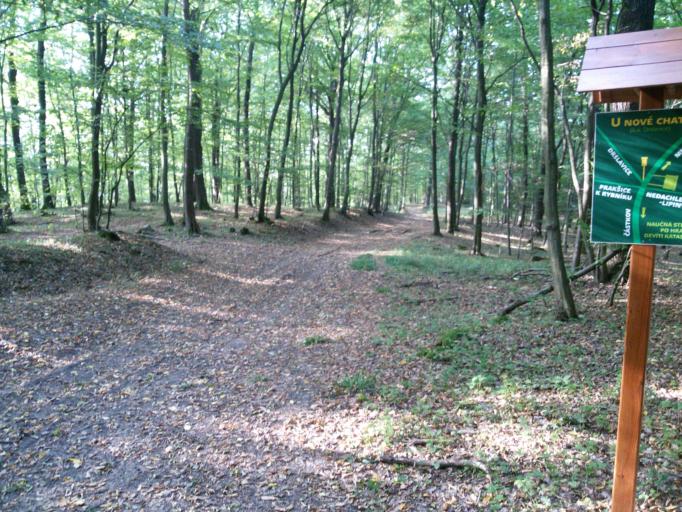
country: CZ
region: Zlin
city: Brezolupy
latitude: 49.0762
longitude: 17.6116
